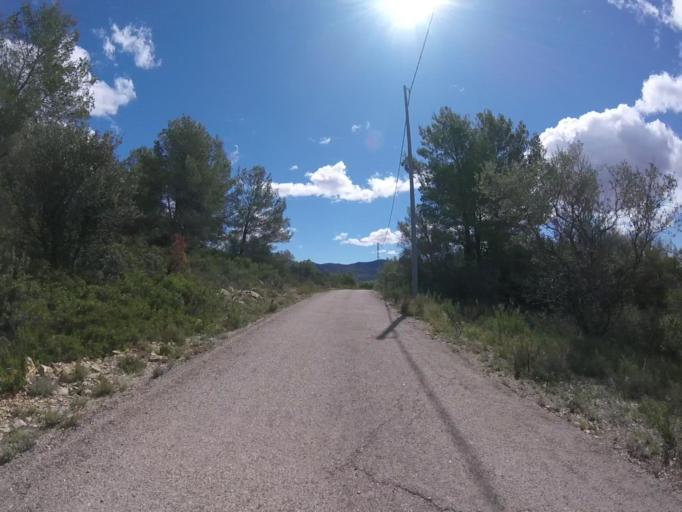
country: ES
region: Valencia
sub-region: Provincia de Castello
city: Sierra-Engarceran
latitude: 40.2703
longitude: -0.0951
